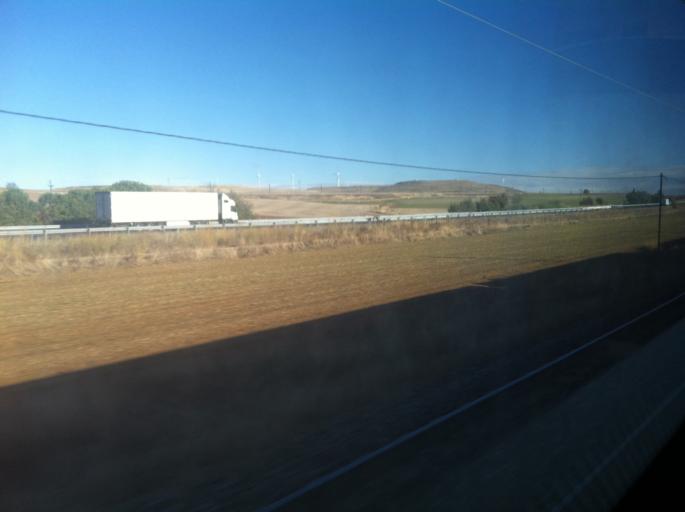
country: ES
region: Castille and Leon
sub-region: Provincia de Burgos
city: Villaverde-Mogina
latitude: 42.1814
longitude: -4.0462
